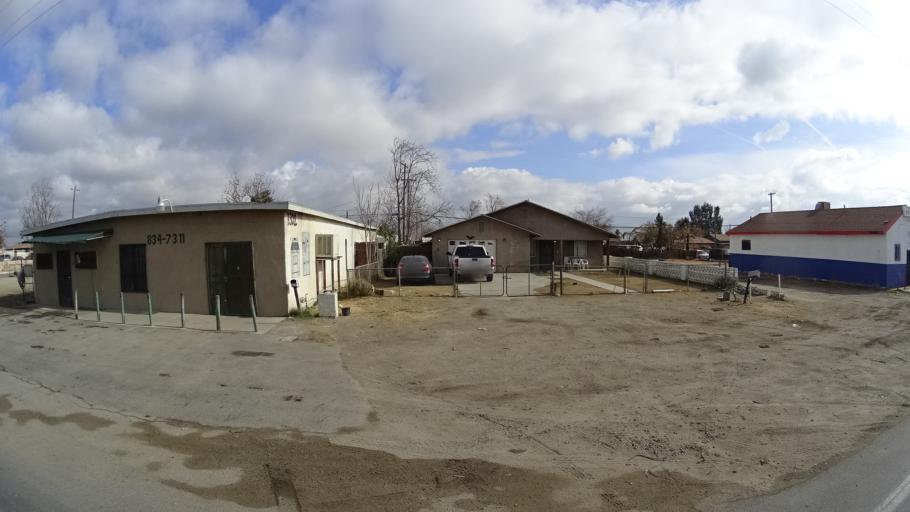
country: US
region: California
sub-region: Kern County
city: Greenfield
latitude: 35.3235
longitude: -118.9855
